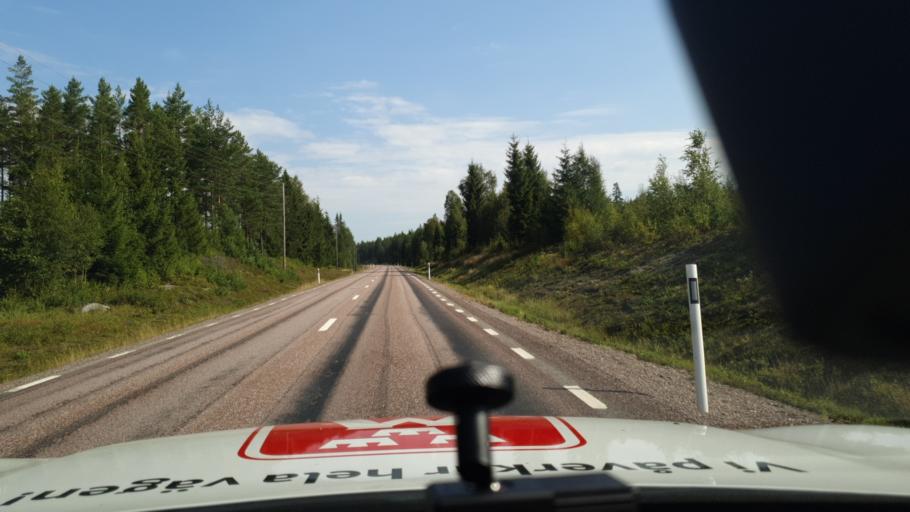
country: SE
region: Vaermland
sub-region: Hagfors Kommun
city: Ekshaerad
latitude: 60.4477
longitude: 13.2812
